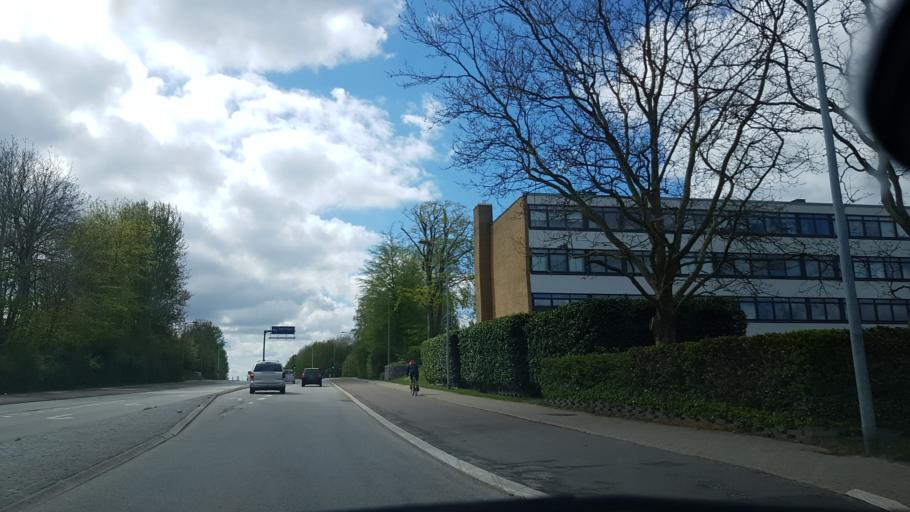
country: DK
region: Capital Region
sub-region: Horsholm Kommune
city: Horsholm
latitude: 55.8784
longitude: 12.4974
